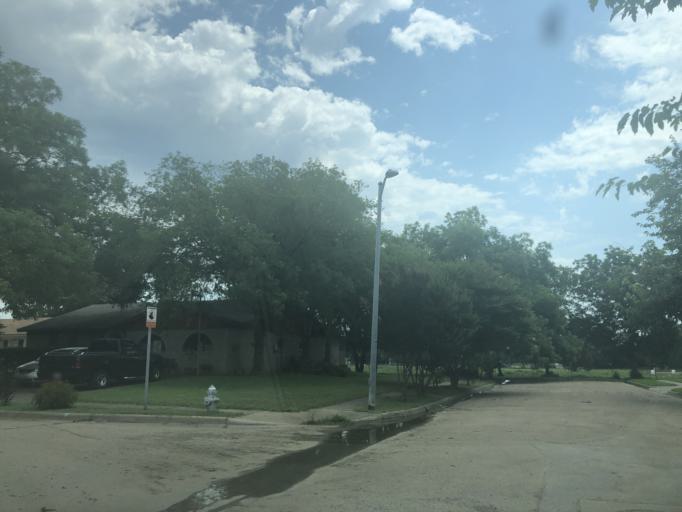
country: US
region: Texas
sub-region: Dallas County
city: Irving
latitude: 32.7908
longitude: -96.9373
